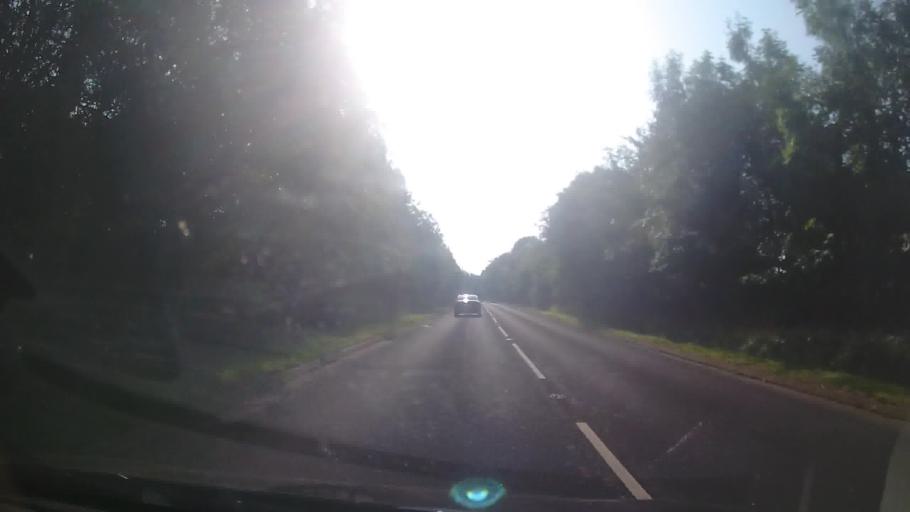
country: GB
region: England
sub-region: Shropshire
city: Bridgnorth
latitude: 52.5348
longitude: -2.4408
